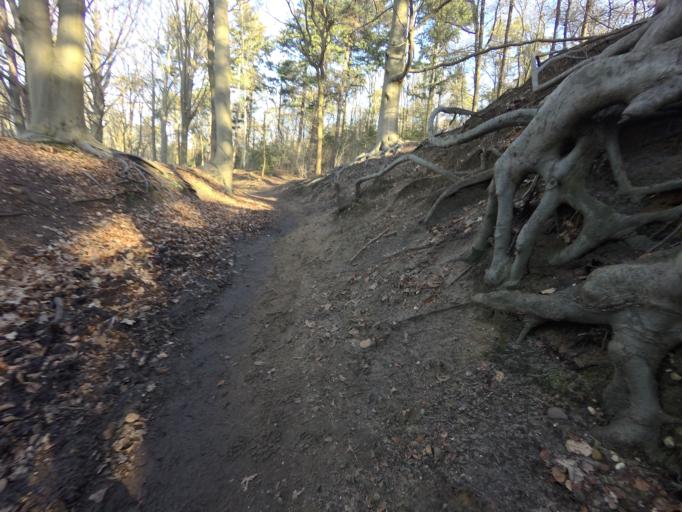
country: NL
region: Gelderland
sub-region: Gemeente Lochem
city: Barchem
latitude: 52.1312
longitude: 6.4352
